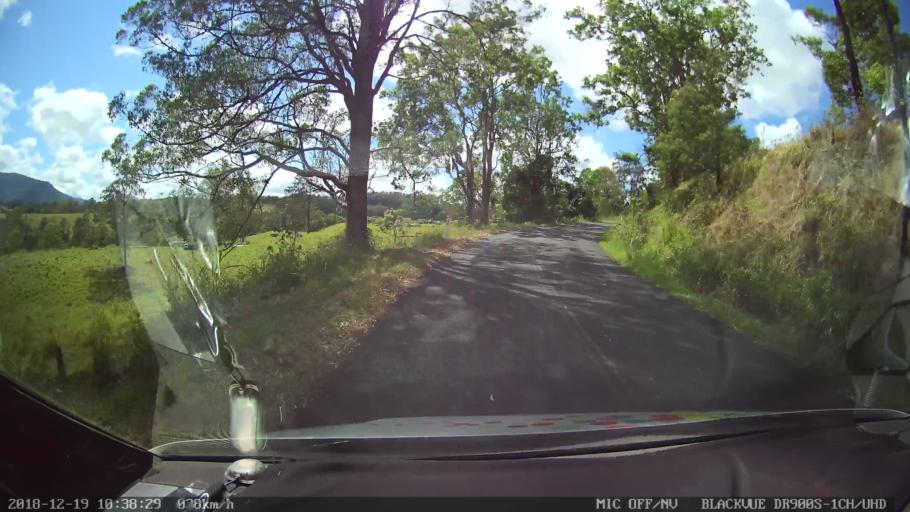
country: AU
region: New South Wales
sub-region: Lismore Municipality
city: Nimbin
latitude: -28.5753
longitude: 153.1544
